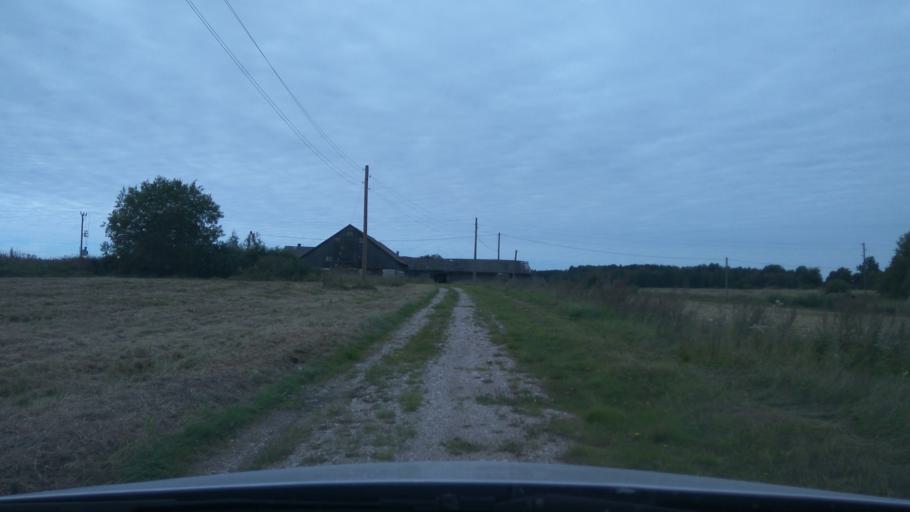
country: LV
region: Kuldigas Rajons
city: Kuldiga
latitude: 57.2439
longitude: 21.9465
